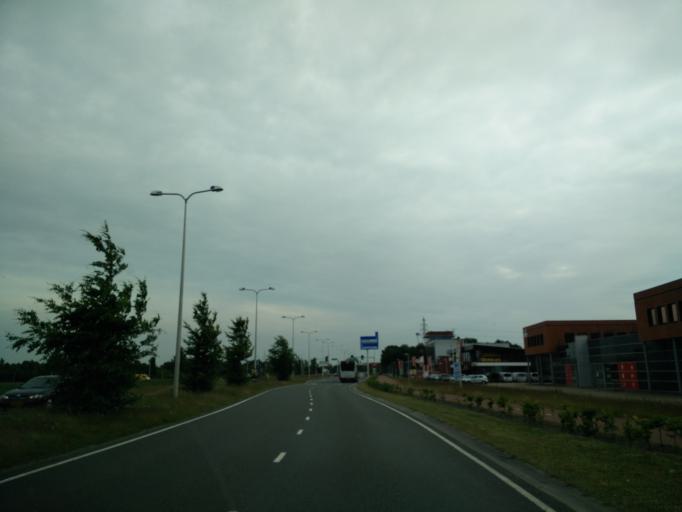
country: NL
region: Drenthe
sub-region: Gemeente Assen
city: Assen
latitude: 53.0247
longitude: 6.5716
